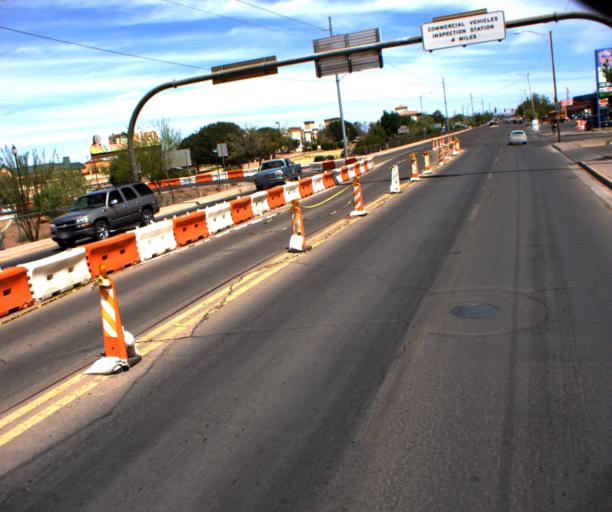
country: MX
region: Sonora
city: Agua Prieta
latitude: 31.3367
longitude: -109.5598
